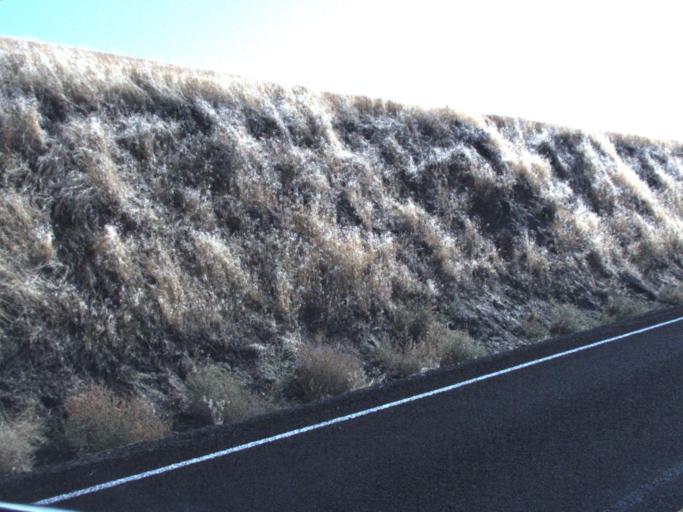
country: US
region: Washington
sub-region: Walla Walla County
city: Waitsburg
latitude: 46.2707
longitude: -118.3498
